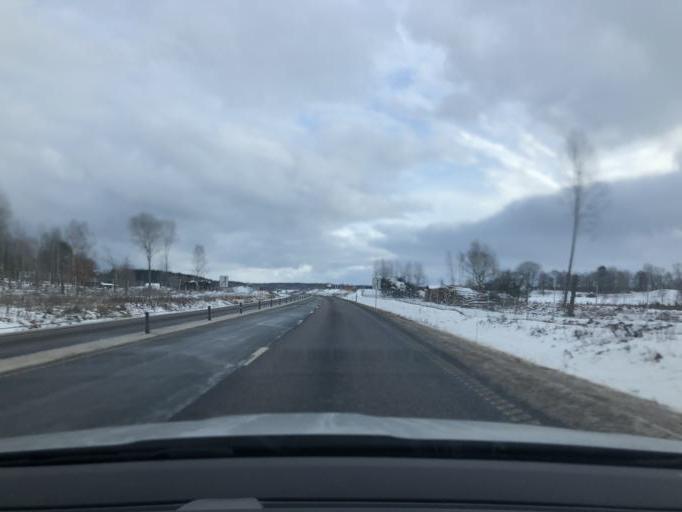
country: SE
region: OEstergoetland
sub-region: Motala Kommun
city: Borensberg
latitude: 58.5858
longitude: 15.1973
